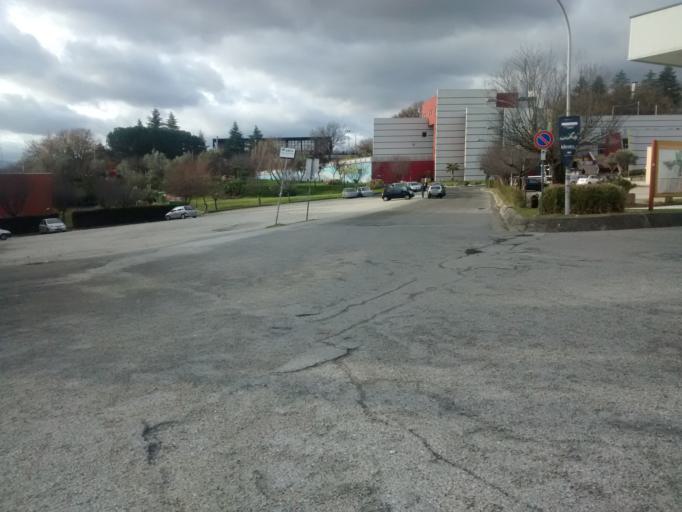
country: IT
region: Calabria
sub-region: Provincia di Cosenza
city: Arcavacata
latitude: 39.3581
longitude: 16.2261
